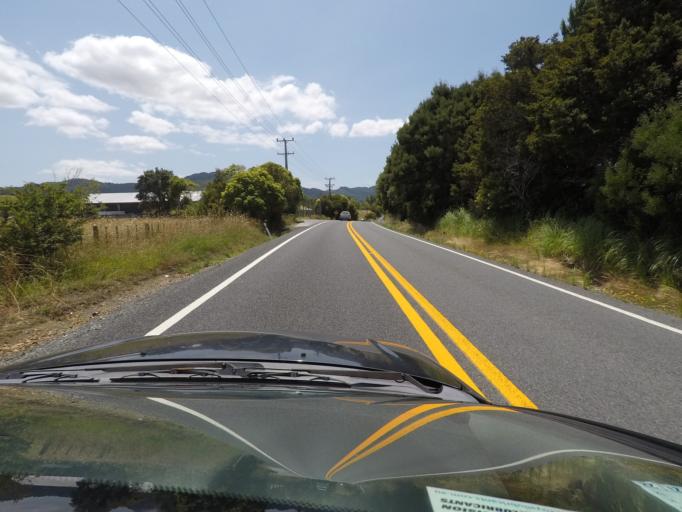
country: NZ
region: Auckland
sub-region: Auckland
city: Warkworth
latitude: -36.3301
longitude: 174.7323
